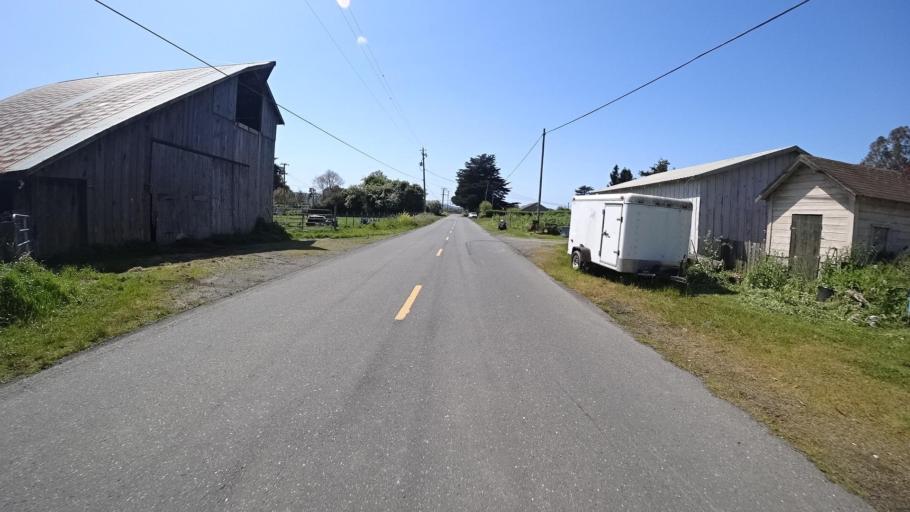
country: US
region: California
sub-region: Humboldt County
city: Fortuna
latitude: 40.5630
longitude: -124.1441
